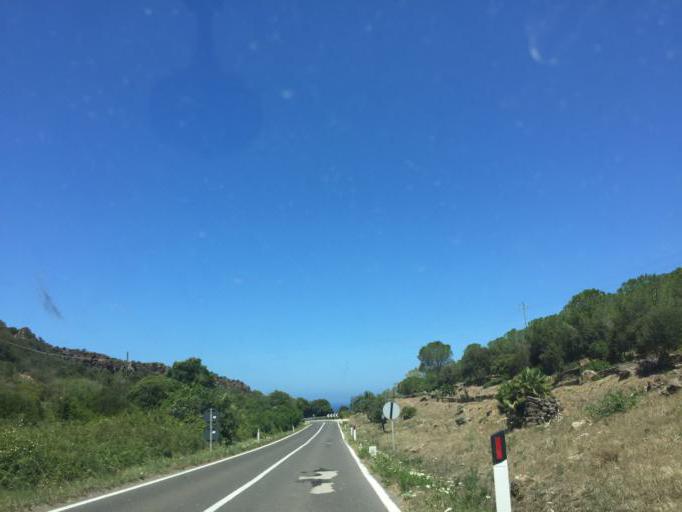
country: IT
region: Sardinia
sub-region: Provincia di Sassari
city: Castelsardo
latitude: 40.8990
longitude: 8.7423
